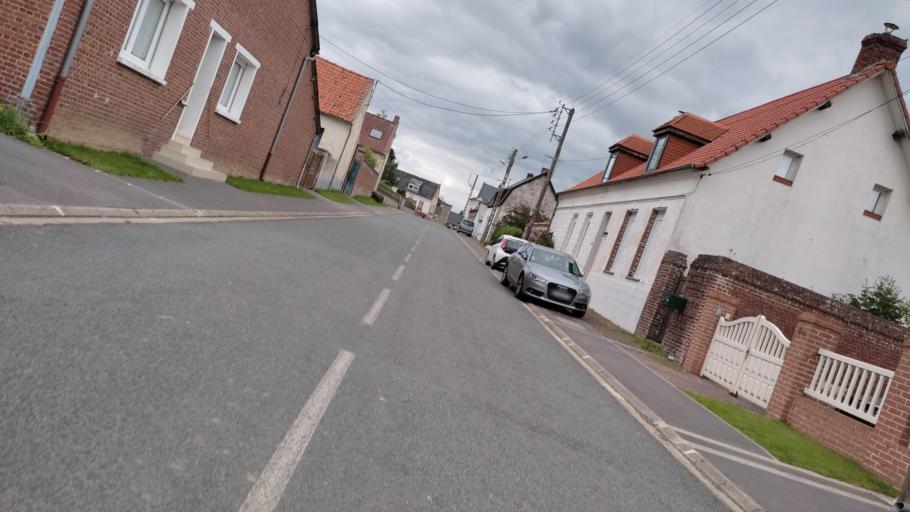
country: FR
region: Nord-Pas-de-Calais
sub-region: Departement du Pas-de-Calais
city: Beaumetz-les-Loges
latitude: 50.2560
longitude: 2.6441
